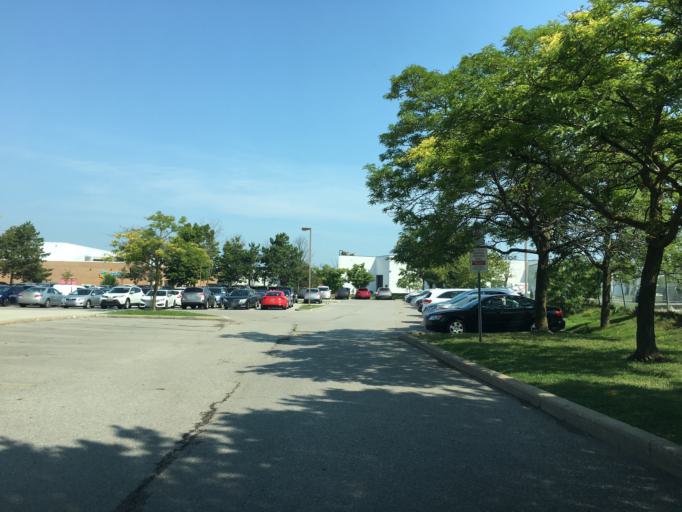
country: CA
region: Ontario
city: Markham
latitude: 43.8216
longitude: -79.3273
